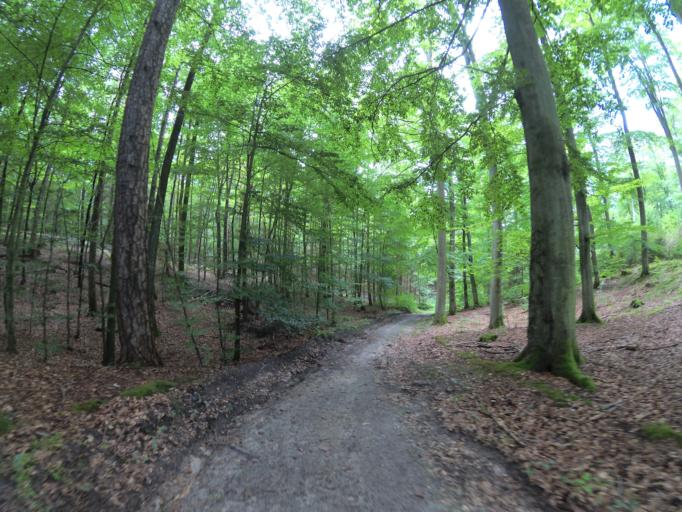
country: PL
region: Pomeranian Voivodeship
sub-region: Gdynia
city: Wielki Kack
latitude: 54.5053
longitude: 18.4478
